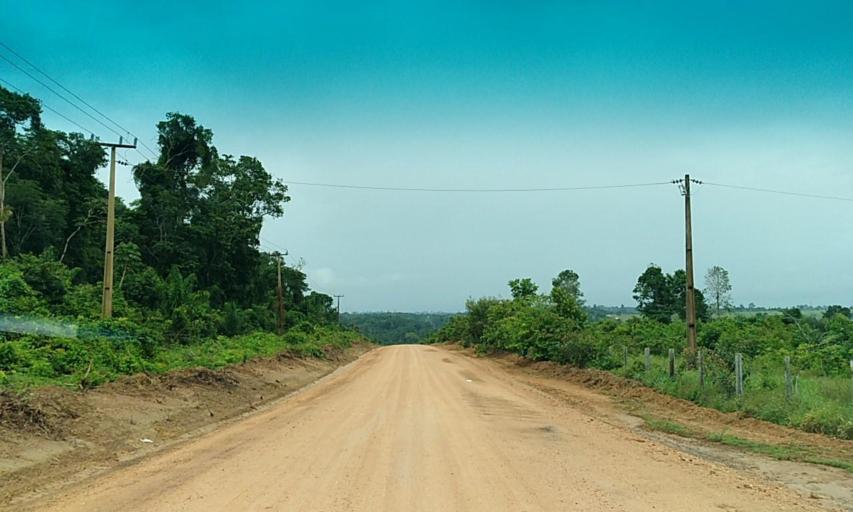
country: BR
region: Para
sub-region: Senador Jose Porfirio
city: Senador Jose Porfirio
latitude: -3.0596
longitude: -51.6536
